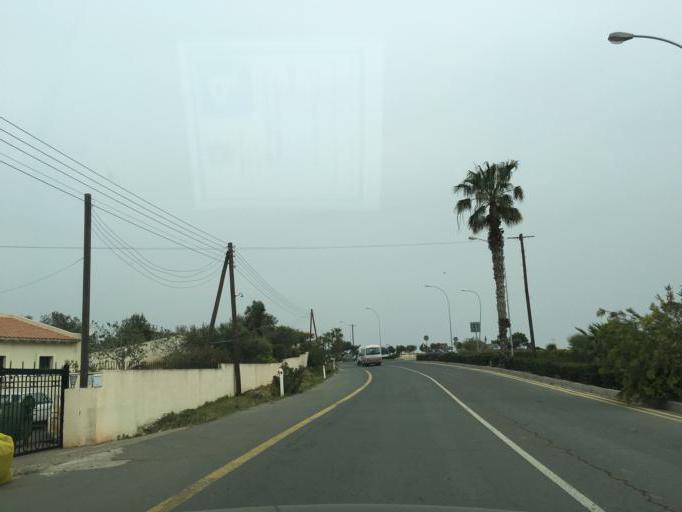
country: CY
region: Ammochostos
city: Ayia Napa
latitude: 34.9870
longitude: 34.0159
